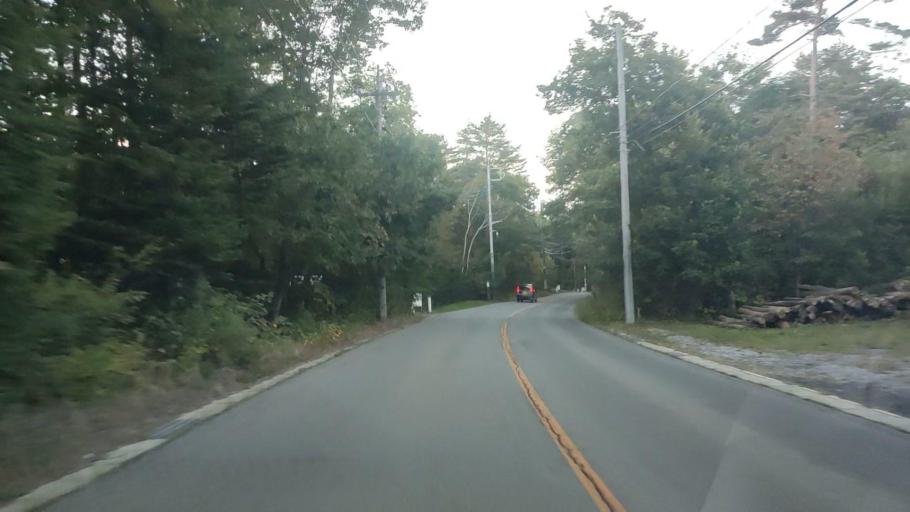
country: JP
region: Nagano
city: Komoro
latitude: 36.4474
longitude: 138.5800
